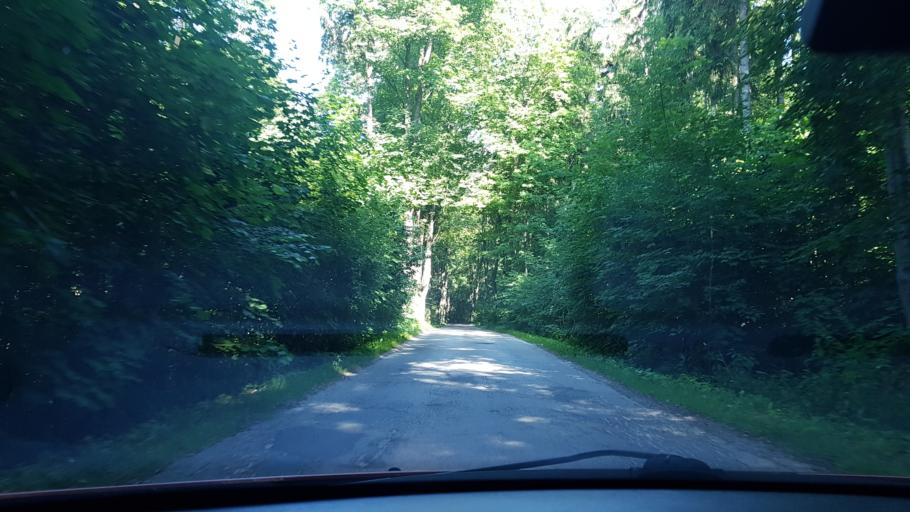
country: PL
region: Lower Silesian Voivodeship
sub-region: Powiat klodzki
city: Miedzylesie
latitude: 50.2307
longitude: 16.7379
